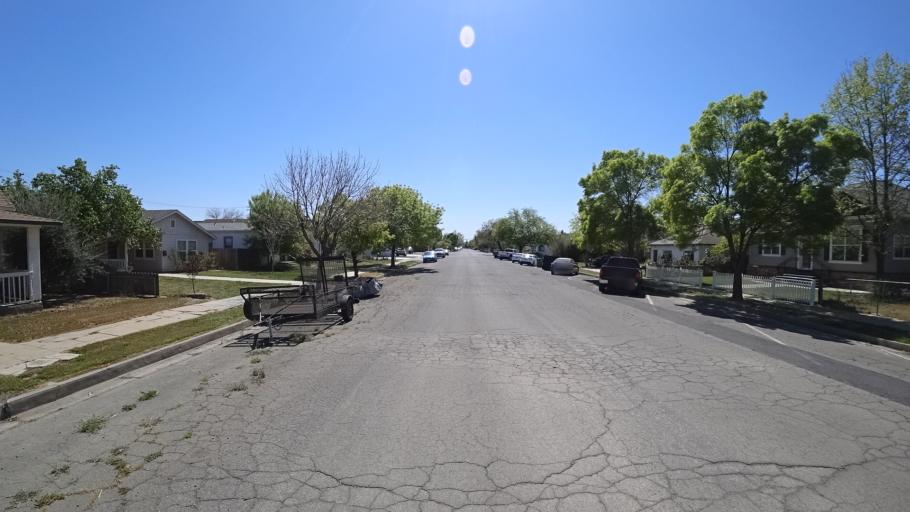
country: US
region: California
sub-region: Glenn County
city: Willows
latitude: 39.5191
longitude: -122.1968
